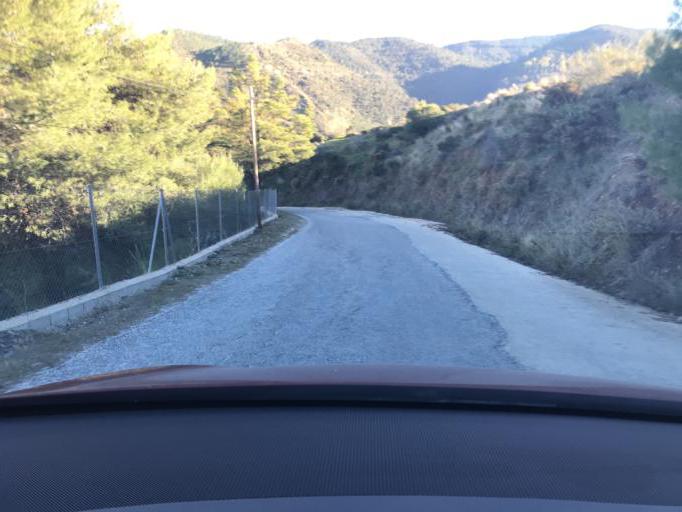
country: ES
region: Andalusia
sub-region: Provincia de Malaga
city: Tolox
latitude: 36.6840
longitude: -4.9109
